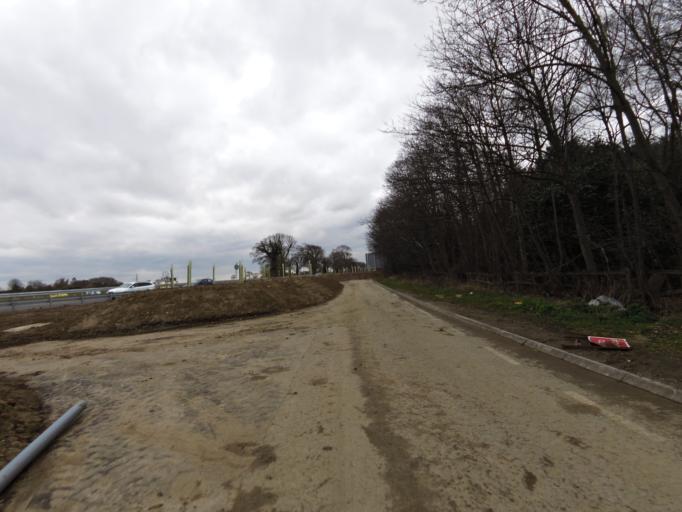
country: GB
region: England
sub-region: Norfolk
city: Hopton on Sea
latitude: 52.5091
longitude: 1.7305
